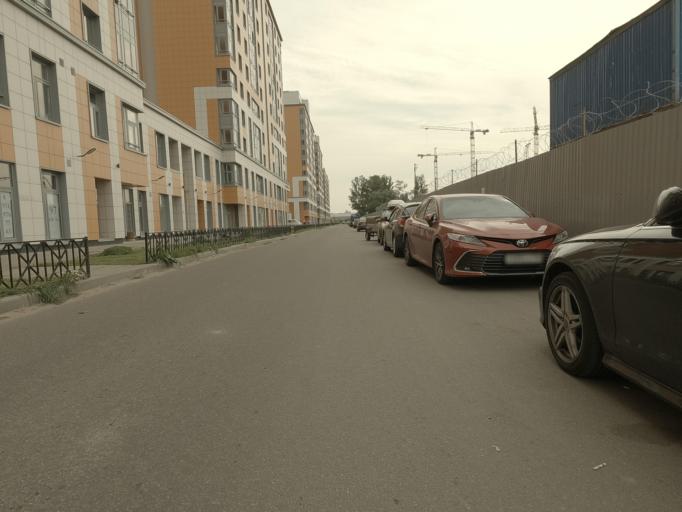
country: RU
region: St.-Petersburg
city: Admiralteisky
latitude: 59.8996
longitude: 30.3072
